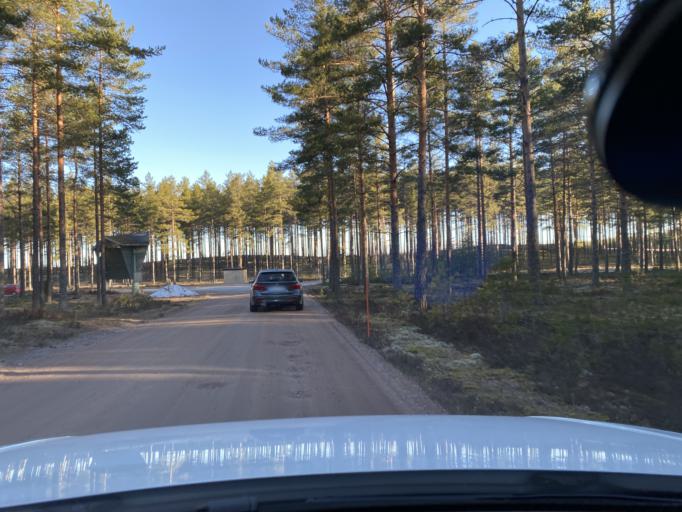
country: FI
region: Satakunta
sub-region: Pori
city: Vampula
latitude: 60.9722
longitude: 22.6710
